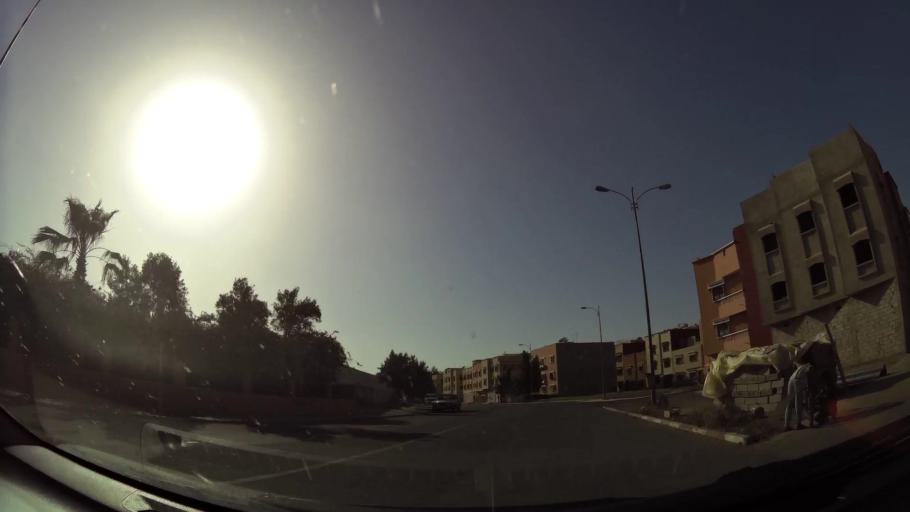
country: MA
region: Souss-Massa-Draa
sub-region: Inezgane-Ait Mellou
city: Inezgane
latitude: 30.3695
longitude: -9.5293
